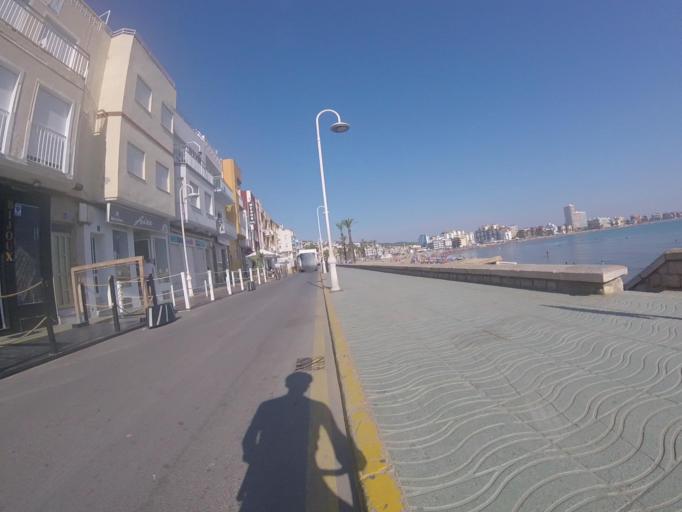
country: ES
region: Valencia
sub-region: Provincia de Castello
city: Peniscola
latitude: 40.3592
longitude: 0.4055
